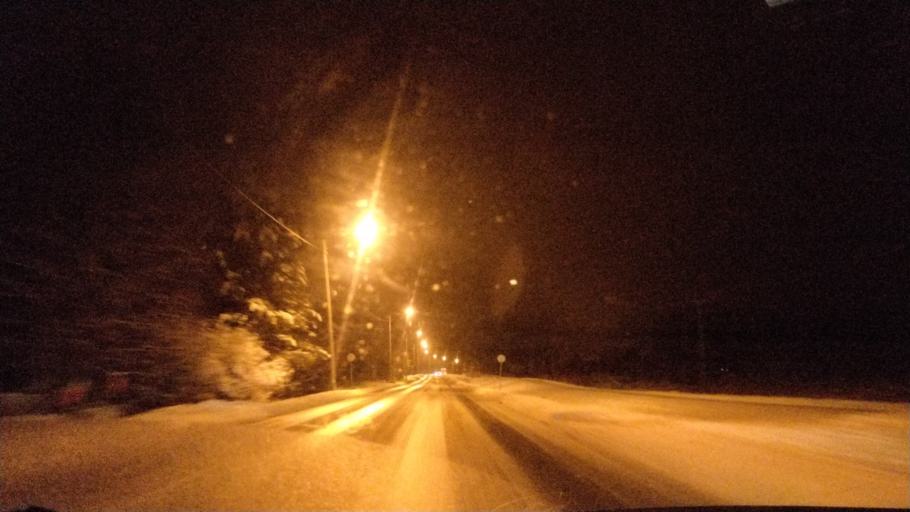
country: FI
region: Lapland
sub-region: Rovaniemi
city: Rovaniemi
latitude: 66.3145
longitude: 25.3619
